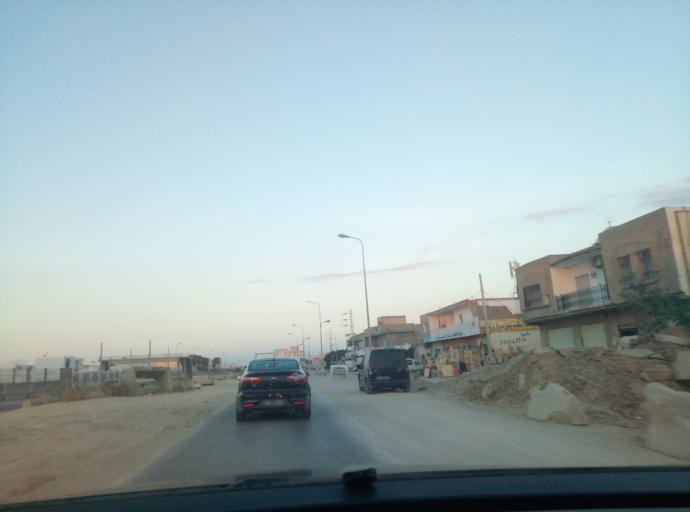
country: TN
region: Manouba
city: Manouba
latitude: 36.7829
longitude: 10.1134
